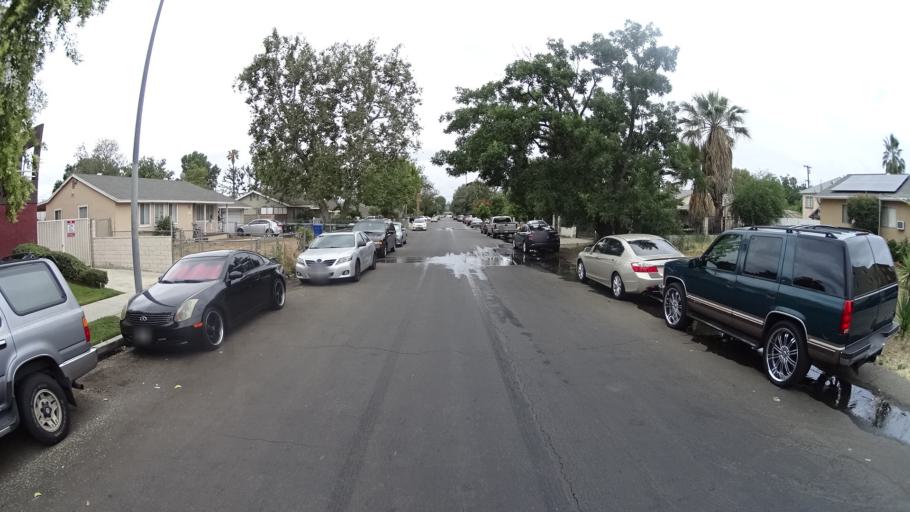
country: US
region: California
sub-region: Los Angeles County
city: San Fernando
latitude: 34.2402
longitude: -118.4515
